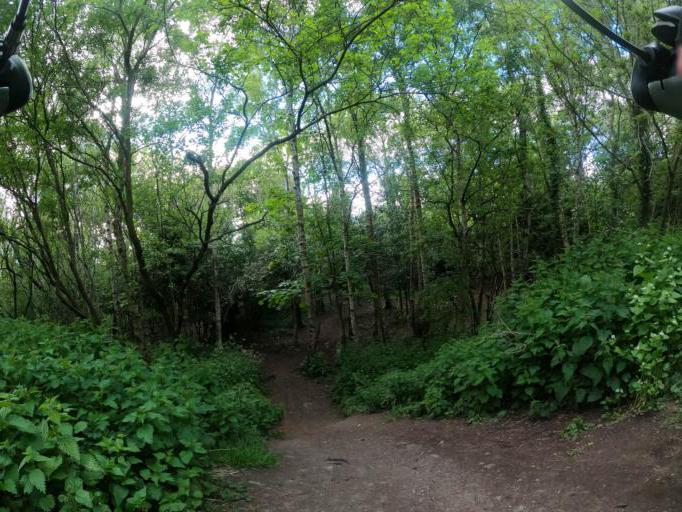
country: GB
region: Scotland
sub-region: Edinburgh
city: Edinburgh
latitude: 55.9743
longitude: -3.2022
